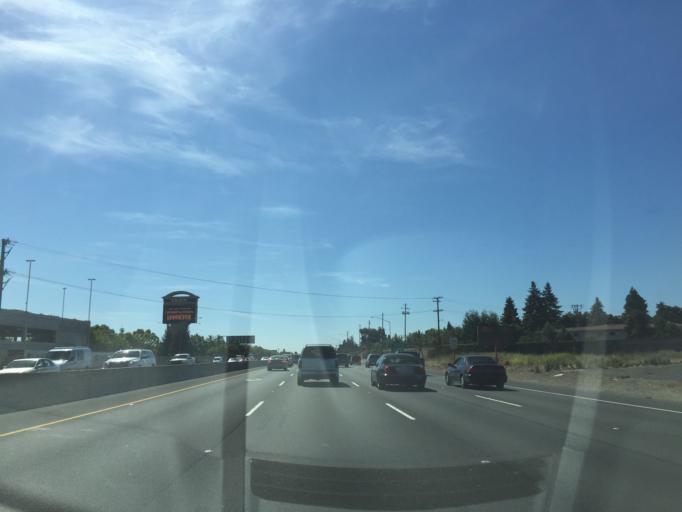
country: US
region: California
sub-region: San Mateo County
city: East Palo Alto
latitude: 37.4599
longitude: -122.1402
